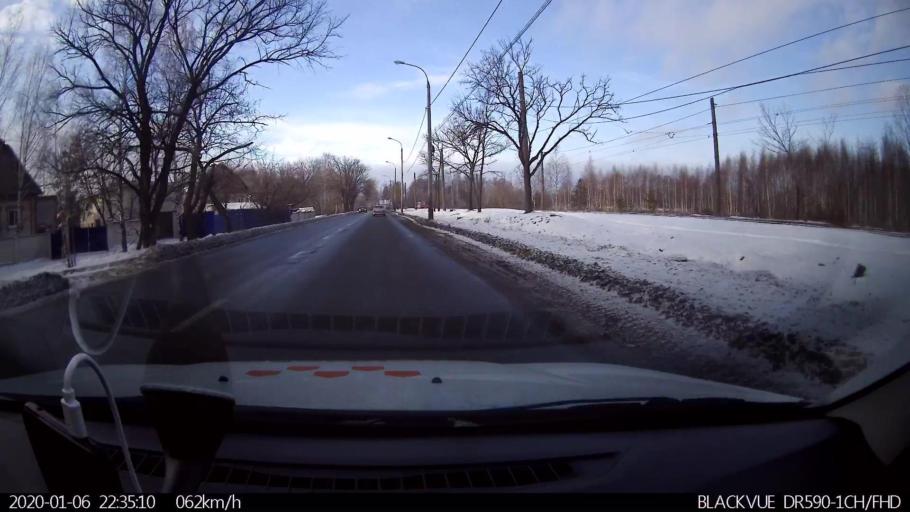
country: RU
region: Nizjnij Novgorod
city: Gorbatovka
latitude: 56.2059
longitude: 43.7748
